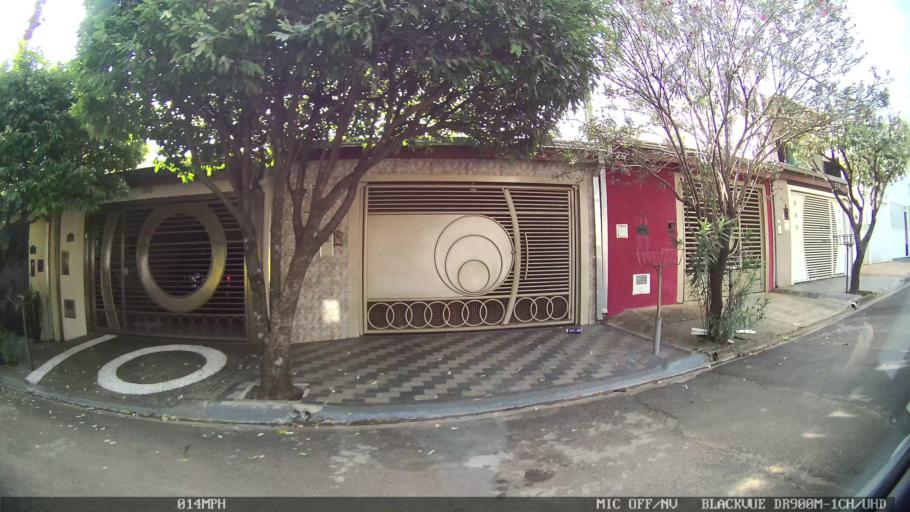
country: BR
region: Sao Paulo
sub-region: Americana
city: Americana
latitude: -22.7177
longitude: -47.3666
